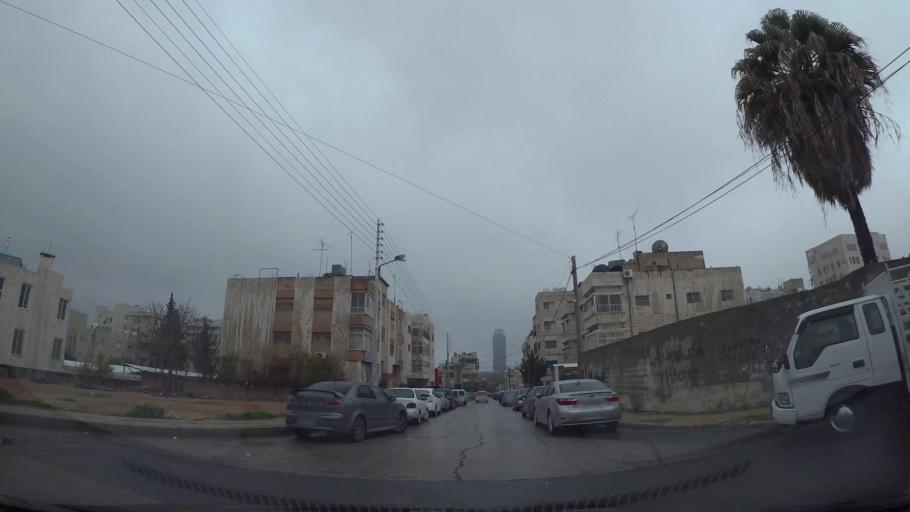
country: JO
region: Amman
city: Amman
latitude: 31.9700
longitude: 35.9165
